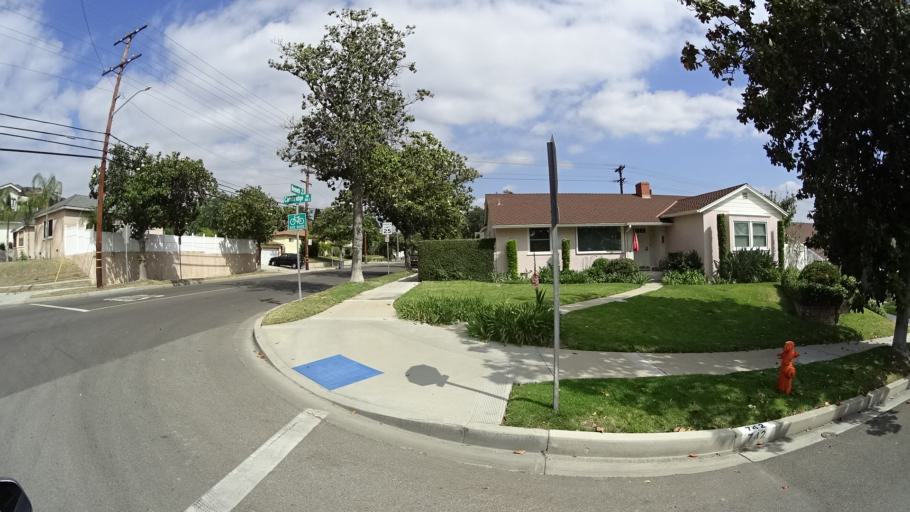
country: US
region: California
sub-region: Los Angeles County
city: Burbank
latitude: 34.1999
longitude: -118.3180
